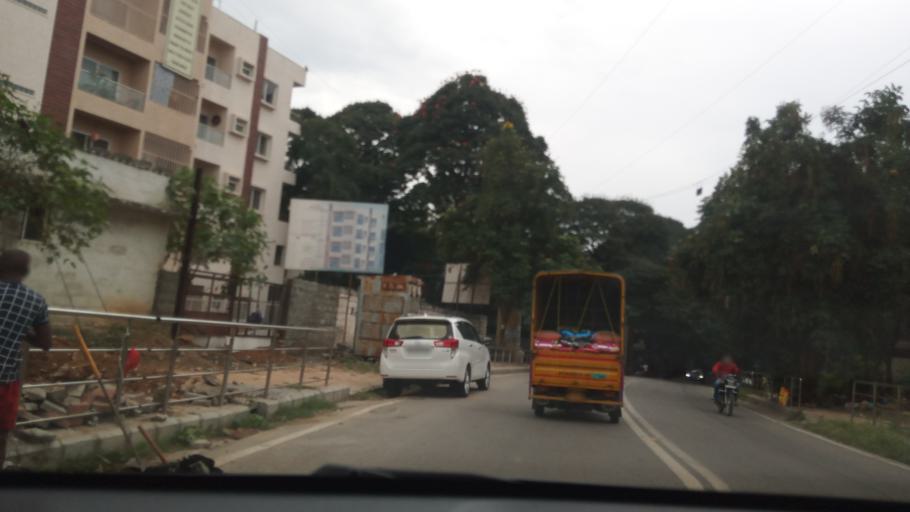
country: IN
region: Karnataka
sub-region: Bangalore Urban
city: Bangalore
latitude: 13.0142
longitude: 77.5387
